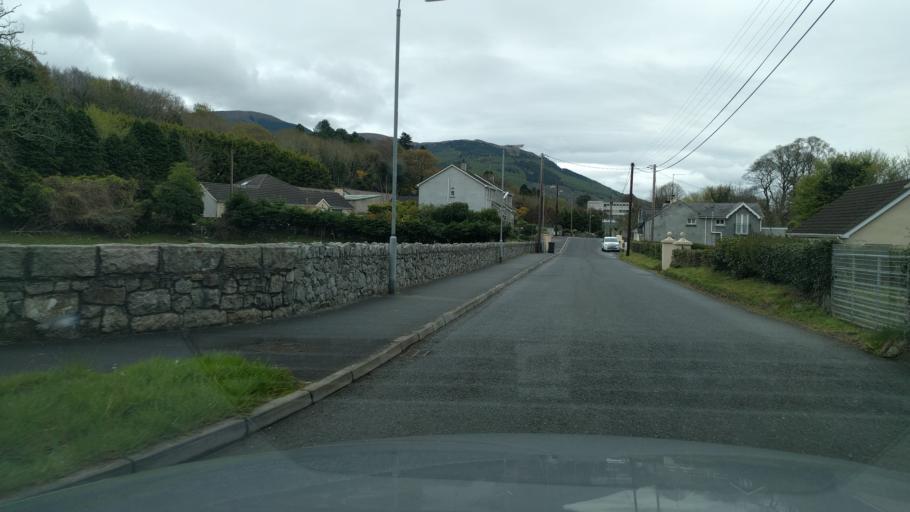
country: GB
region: Northern Ireland
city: Rostrevor
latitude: 54.1078
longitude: -6.2044
